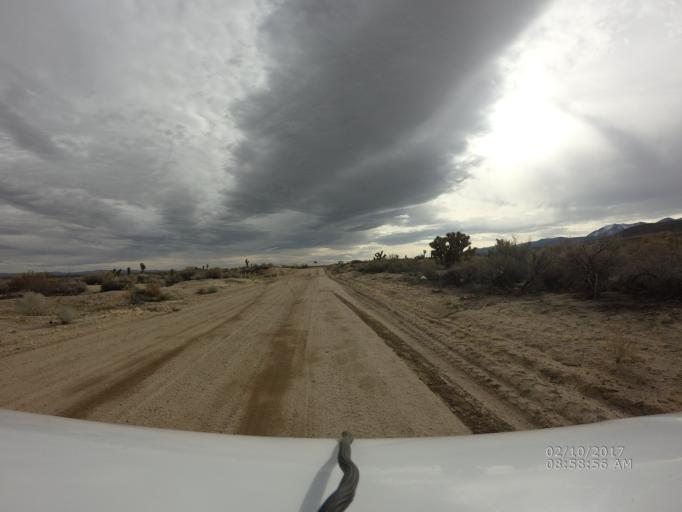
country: US
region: California
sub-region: Los Angeles County
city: Littlerock
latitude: 34.4918
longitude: -117.8891
